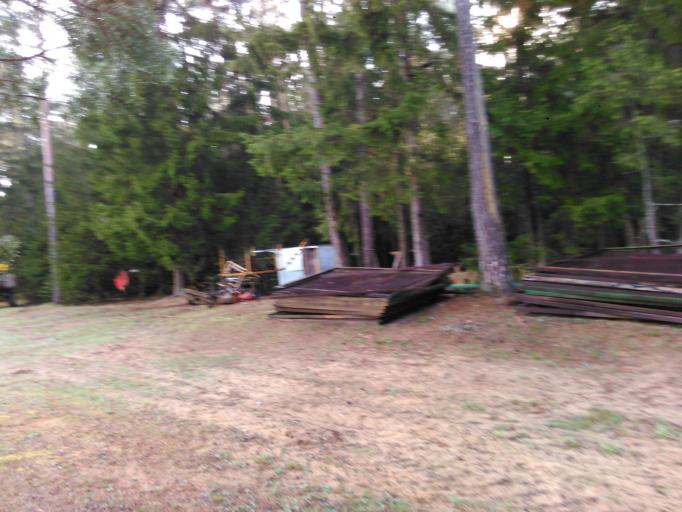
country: BY
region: Minsk
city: Rakaw
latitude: 53.9687
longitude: 27.0158
